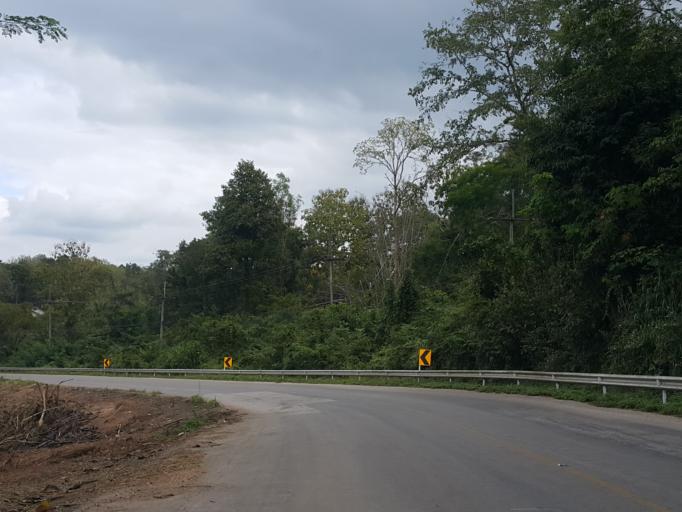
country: TH
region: Lampang
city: Chae Hom
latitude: 18.5939
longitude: 99.4772
